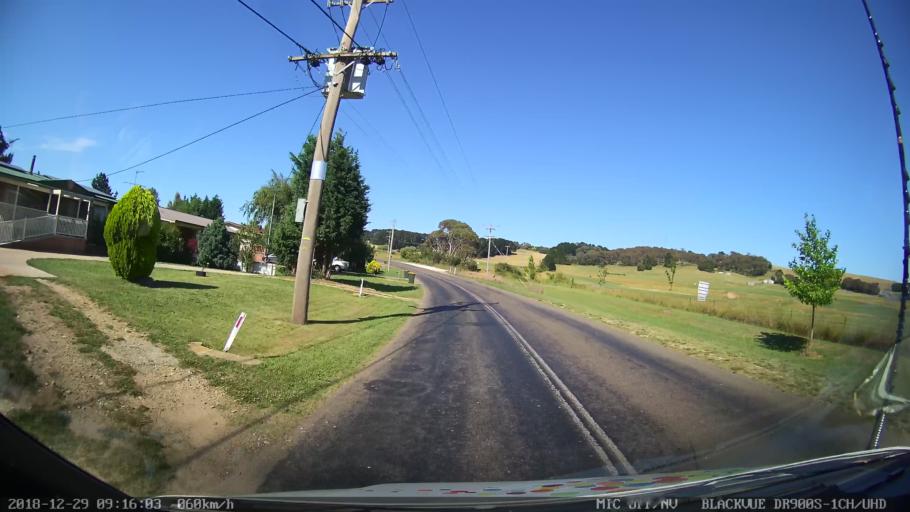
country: AU
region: New South Wales
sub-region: Upper Lachlan Shire
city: Crookwell
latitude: -34.4560
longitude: 149.4547
